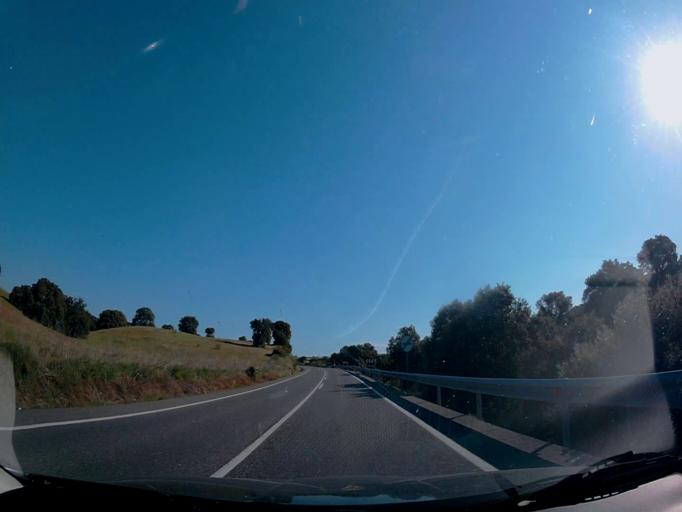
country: ES
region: Castille-La Mancha
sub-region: Province of Toledo
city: Escalona
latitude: 40.1971
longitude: -4.3997
